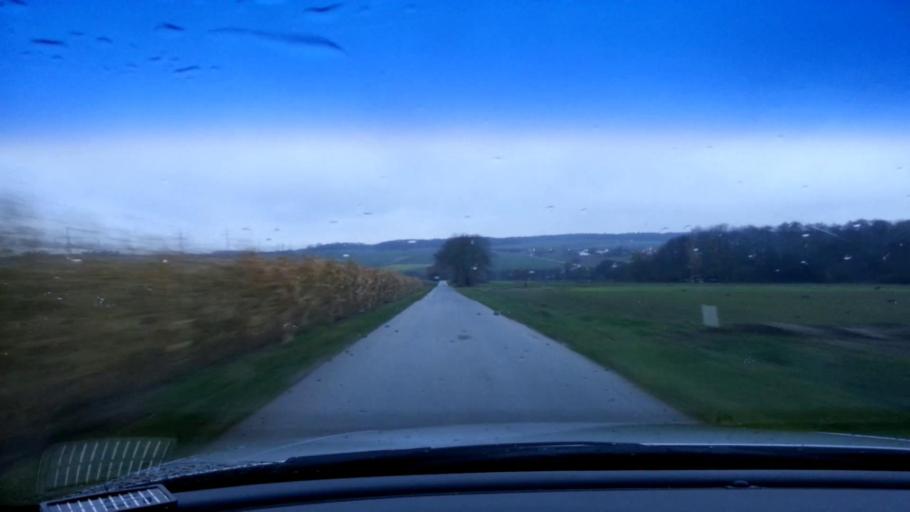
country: DE
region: Bavaria
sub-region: Upper Franconia
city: Memmelsdorf
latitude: 49.9581
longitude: 10.9718
